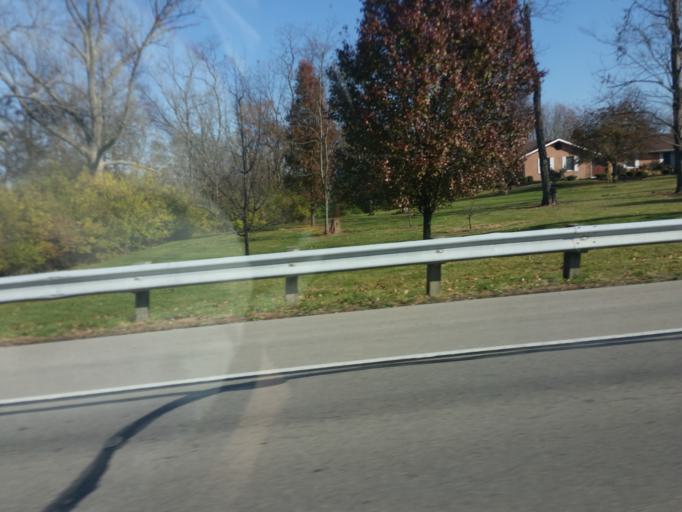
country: US
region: Ohio
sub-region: Butler County
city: Oxford
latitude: 39.4402
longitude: -84.6812
